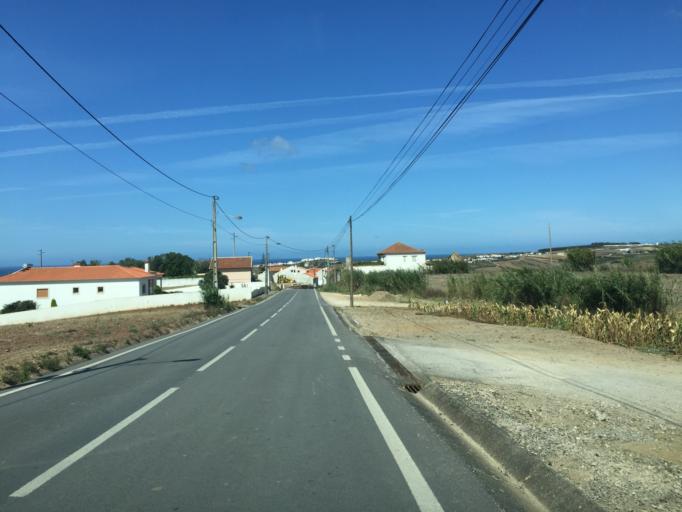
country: PT
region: Lisbon
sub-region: Lourinha
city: Lourinha
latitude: 39.2698
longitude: -9.3038
